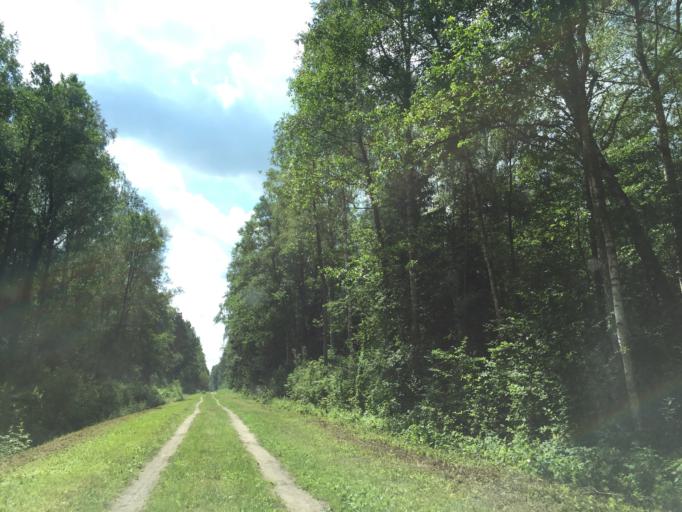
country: LV
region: Ozolnieku
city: Ozolnieki
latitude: 56.6822
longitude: 23.7527
